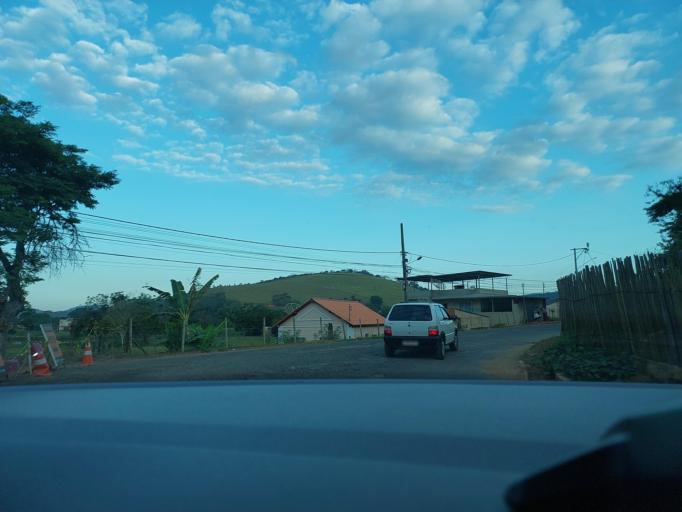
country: BR
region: Rio de Janeiro
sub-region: Natividade
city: Natividade
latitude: -21.1826
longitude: -42.1033
